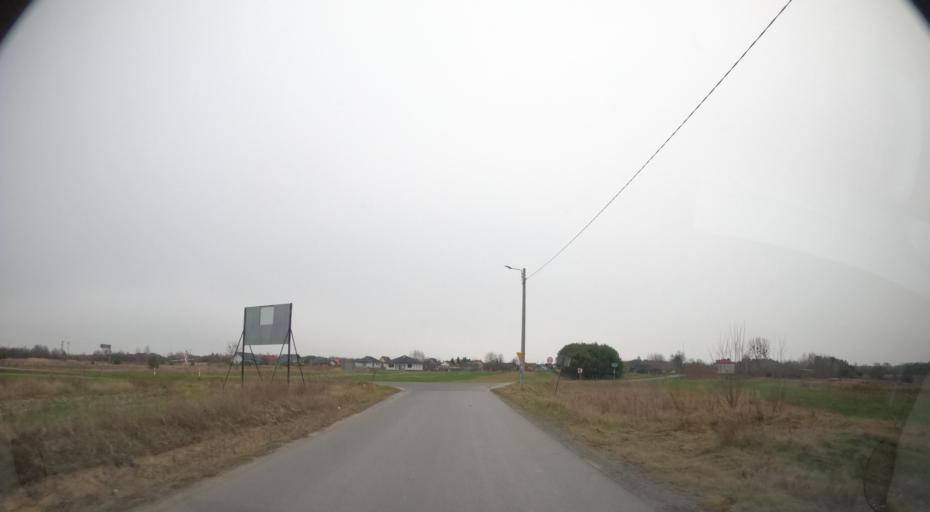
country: PL
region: Masovian Voivodeship
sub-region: Powiat radomski
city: Jastrzebia
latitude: 51.4723
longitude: 21.2001
